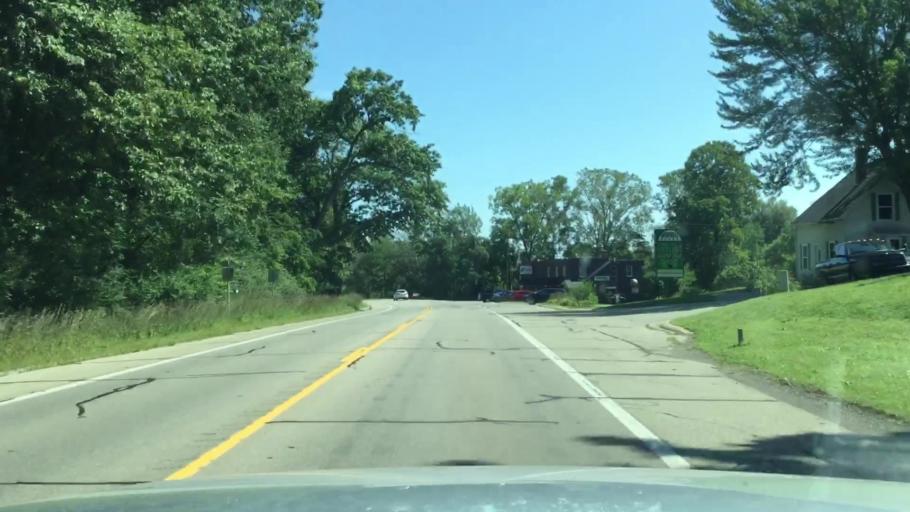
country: US
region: Michigan
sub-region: Washtenaw County
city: Manchester
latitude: 42.0595
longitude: -84.1279
